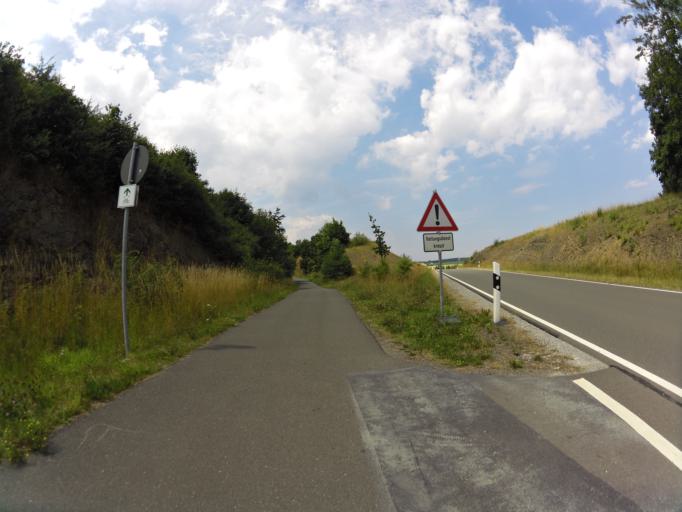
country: DE
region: Thuringia
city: Gorkwitz
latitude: 50.5673
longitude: 11.7676
